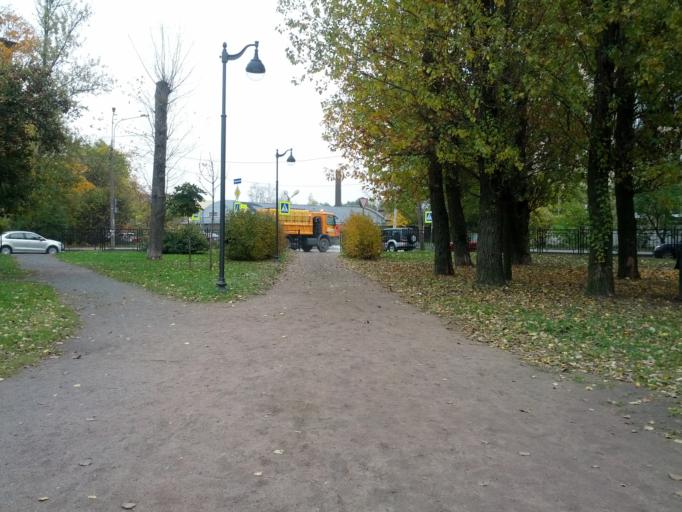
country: RU
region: St.-Petersburg
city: Obukhovo
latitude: 59.8931
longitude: 30.4189
